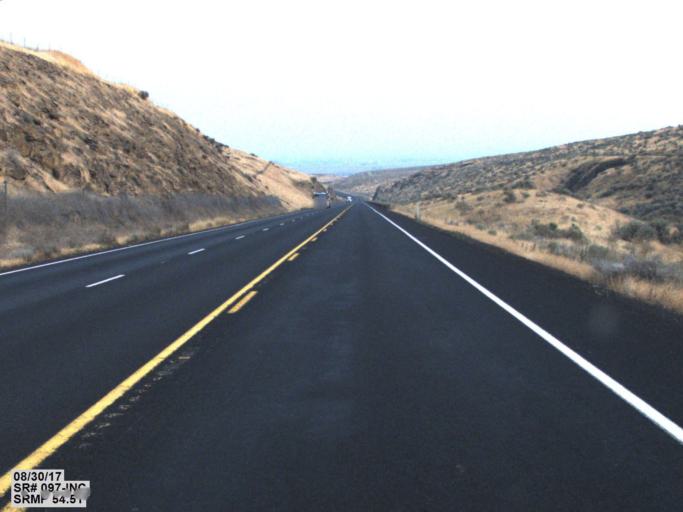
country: US
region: Washington
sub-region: Yakima County
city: Toppenish
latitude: 46.2837
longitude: -120.3647
